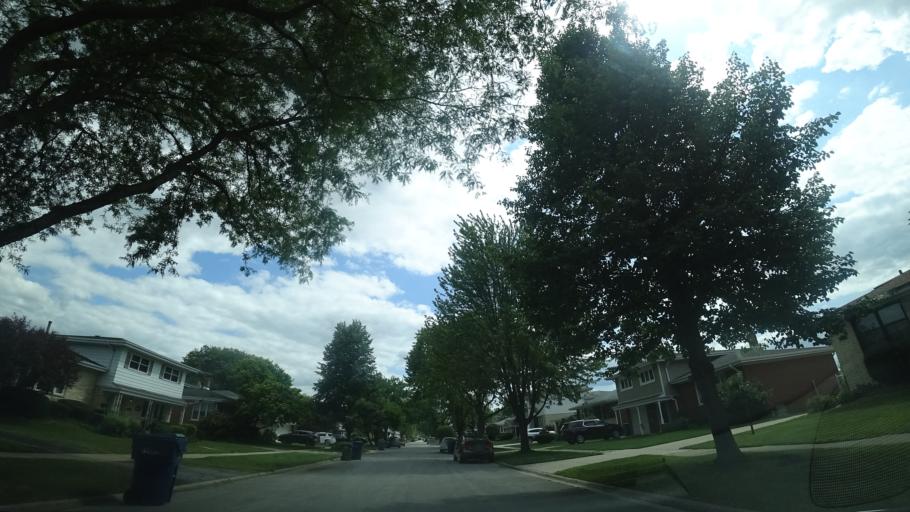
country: US
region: Illinois
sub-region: Cook County
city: Alsip
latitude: 41.6963
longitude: -87.7339
